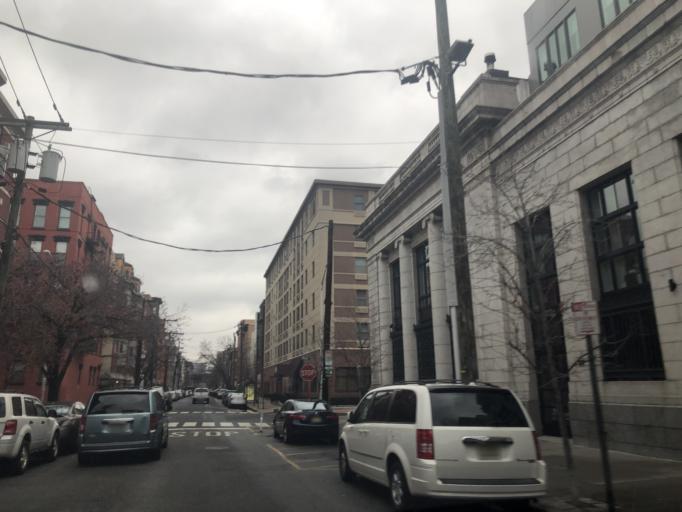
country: US
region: New Jersey
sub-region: Hudson County
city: Hoboken
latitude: 40.7379
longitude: -74.0355
